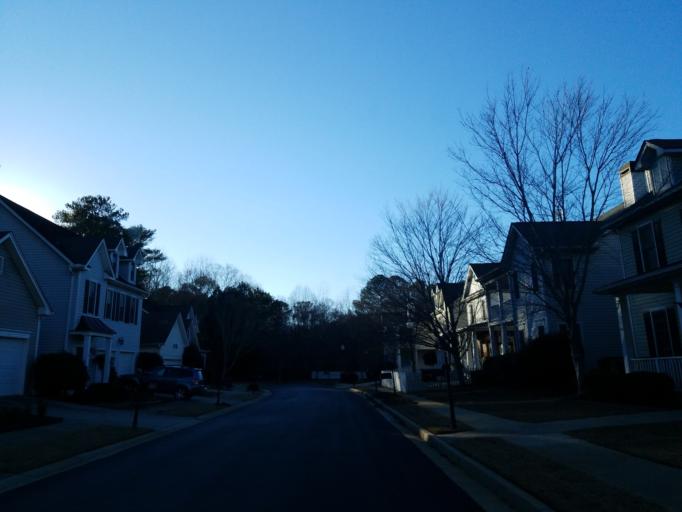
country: US
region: Georgia
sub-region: Cobb County
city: Smyrna
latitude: 33.9341
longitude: -84.4848
